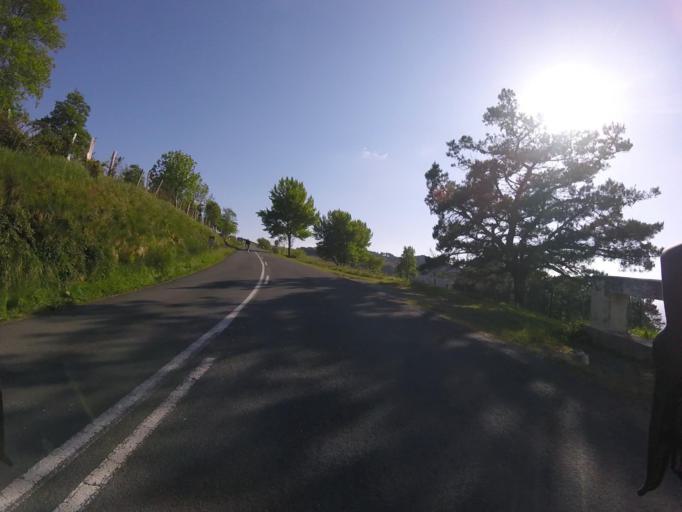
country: ES
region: Basque Country
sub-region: Provincia de Guipuzcoa
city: Fuenterrabia
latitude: 43.3592
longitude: -1.8395
